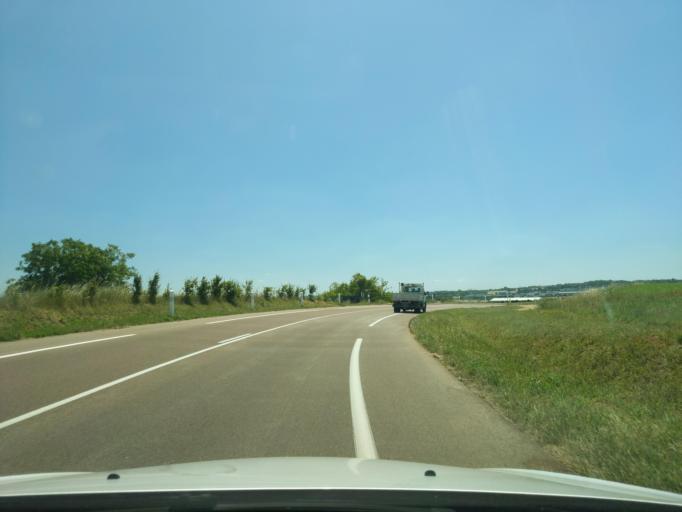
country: FR
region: Bourgogne
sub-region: Departement de la Cote-d'Or
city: Ruffey-les-Echirey
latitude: 47.3696
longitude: 5.0732
